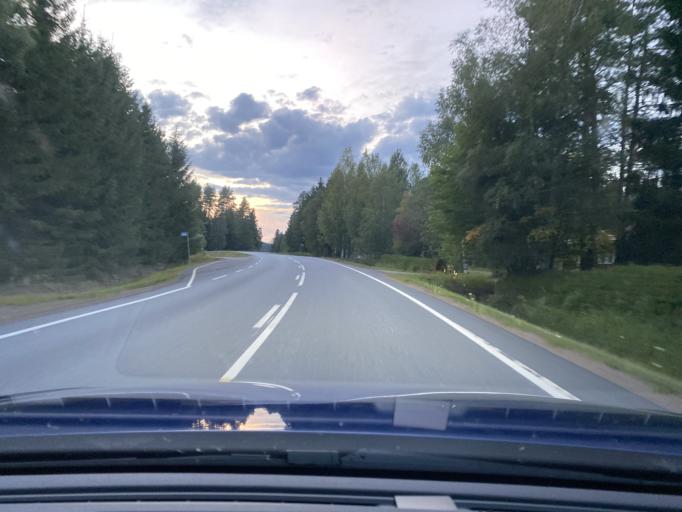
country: FI
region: Satakunta
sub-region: Pohjois-Satakunta
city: Honkajoki
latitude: 62.2183
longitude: 22.2871
